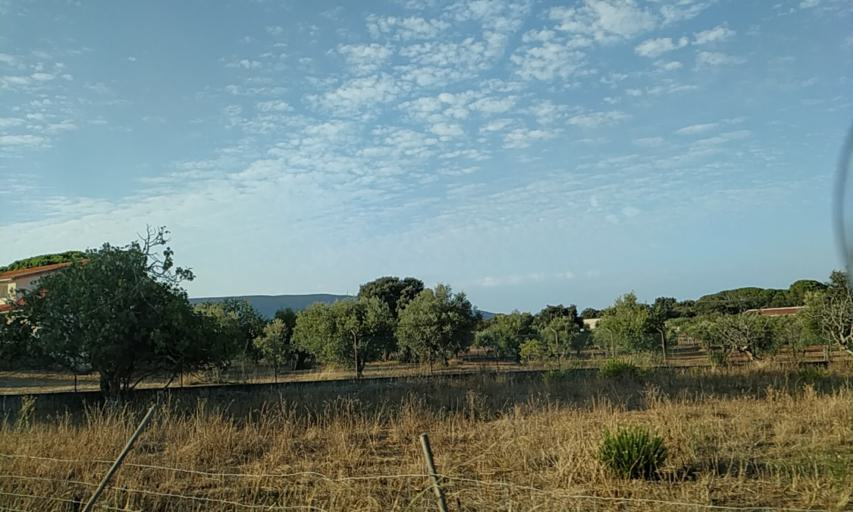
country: PT
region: Santarem
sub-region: Alcanena
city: Alcanena
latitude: 39.4577
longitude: -8.6343
